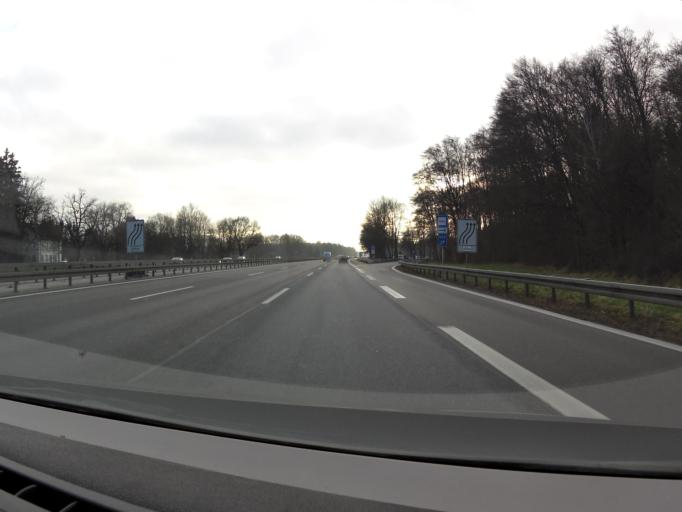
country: DE
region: Bavaria
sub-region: Upper Bavaria
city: Schaftlarn
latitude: 48.0313
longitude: 11.4277
